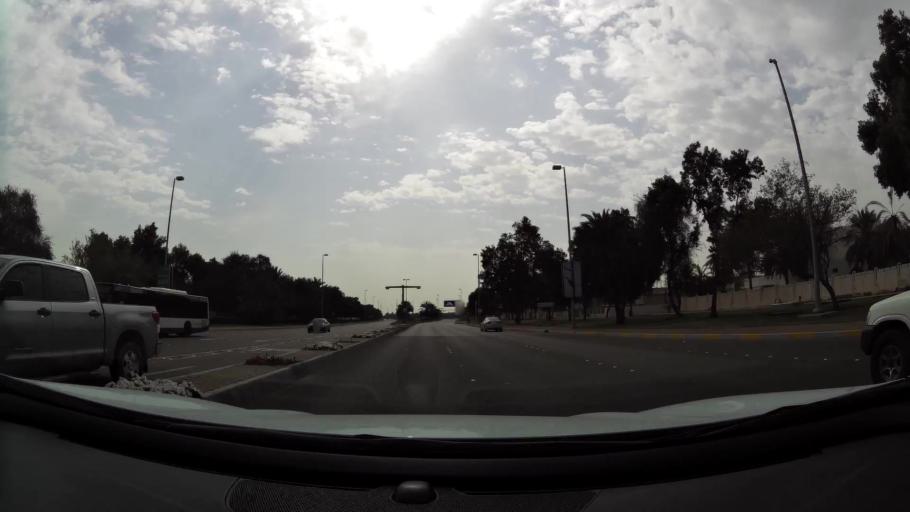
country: AE
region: Abu Dhabi
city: Abu Dhabi
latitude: 24.4394
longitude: 54.3718
